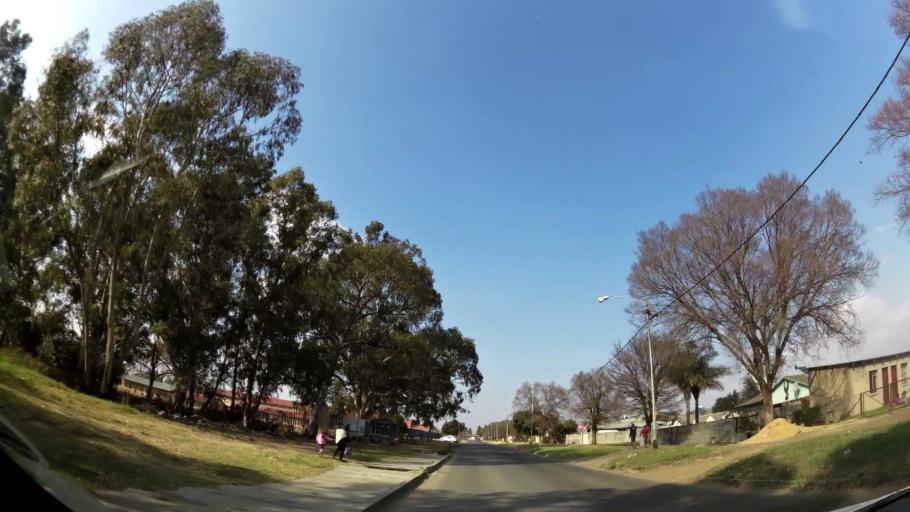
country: ZA
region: Gauteng
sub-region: City of Johannesburg Metropolitan Municipality
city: Modderfontein
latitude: -26.1558
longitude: 28.2048
